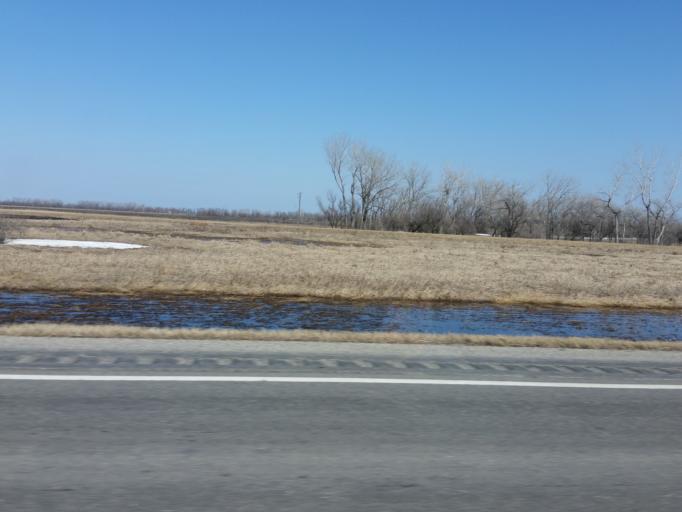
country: US
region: North Dakota
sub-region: Grand Forks County
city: Grand Forks Air Force Base
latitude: 48.1566
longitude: -97.2782
